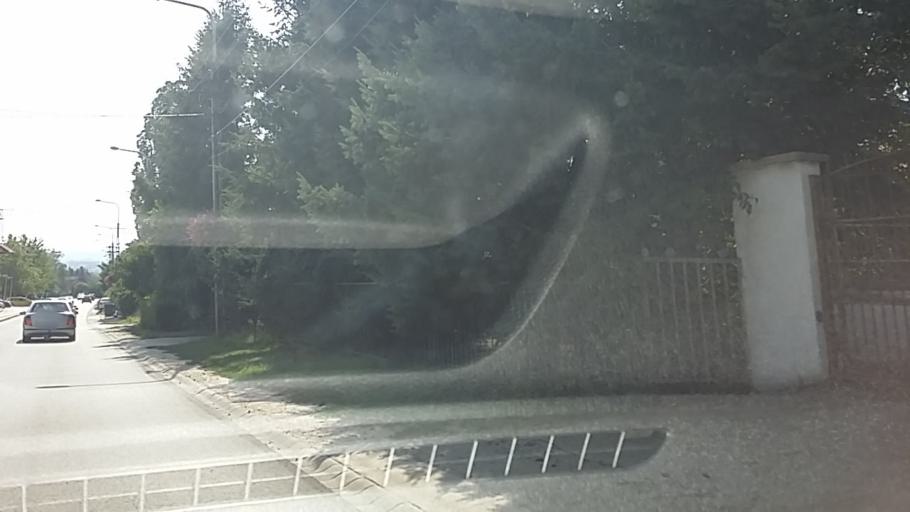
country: HU
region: Pest
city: Erdokertes
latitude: 47.6688
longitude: 19.3050
